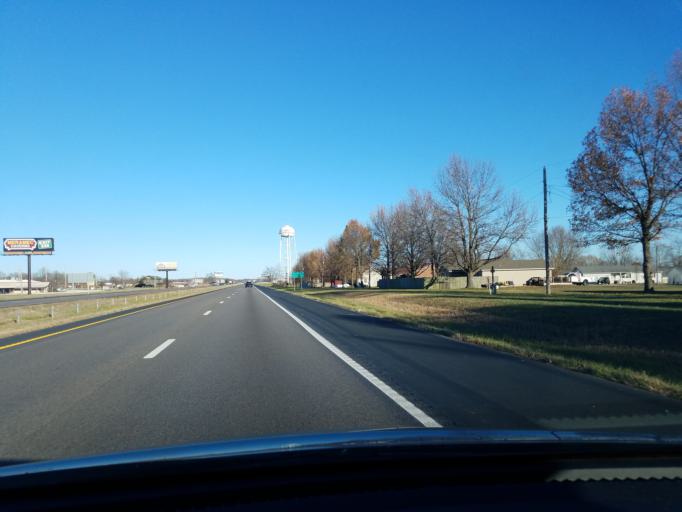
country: US
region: Missouri
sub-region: Phelps County
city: Saint James
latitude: 38.0090
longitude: -91.6081
